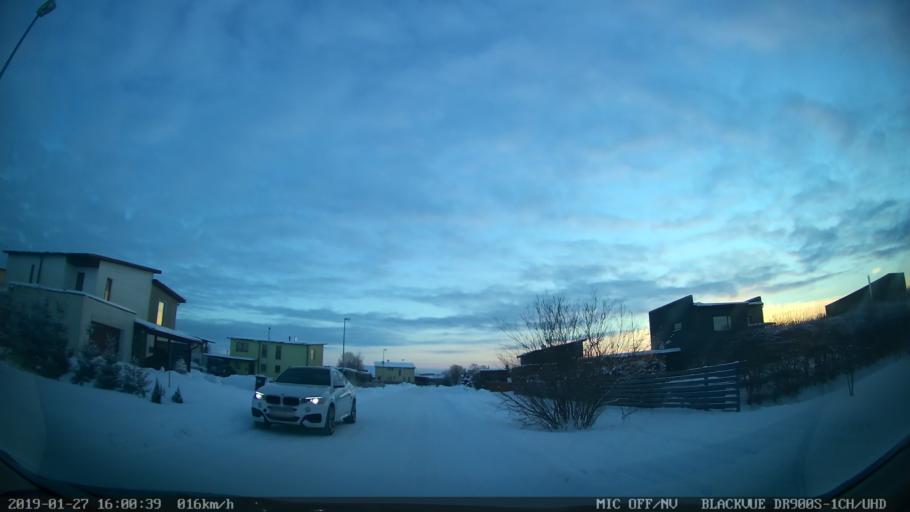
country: EE
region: Harju
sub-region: Tallinna linn
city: Tallinn
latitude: 59.3981
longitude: 24.8003
